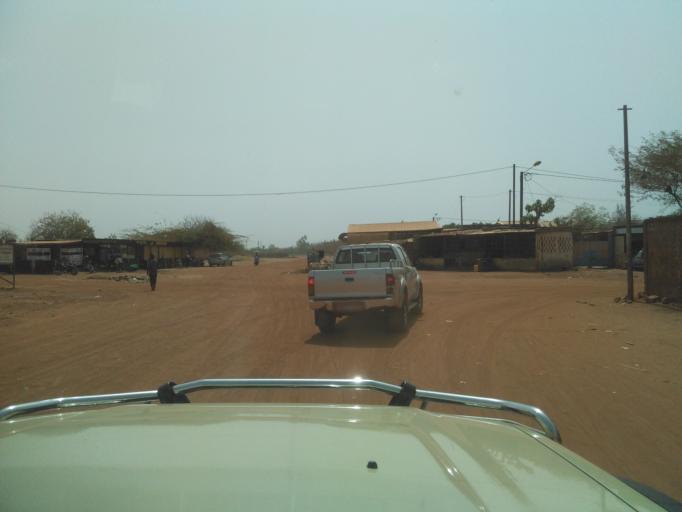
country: BF
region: Centre
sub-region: Kadiogo Province
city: Ouagadougou
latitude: 12.3816
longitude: -1.4752
